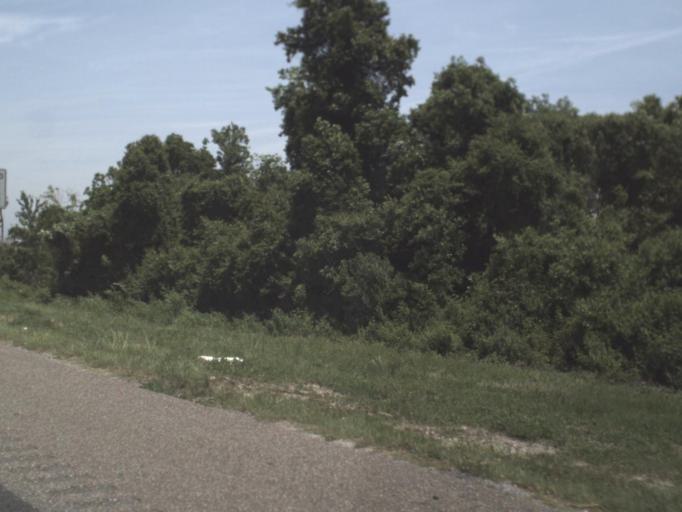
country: US
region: Florida
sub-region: Duval County
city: Jacksonville
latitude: 30.3639
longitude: -81.5525
